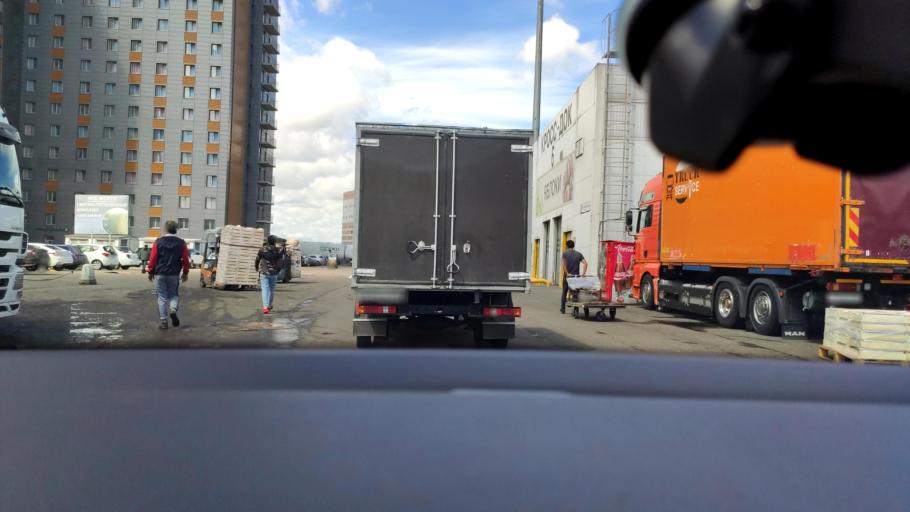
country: RU
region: Moskovskaya
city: Mosrentgen
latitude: 55.5971
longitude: 37.4654
